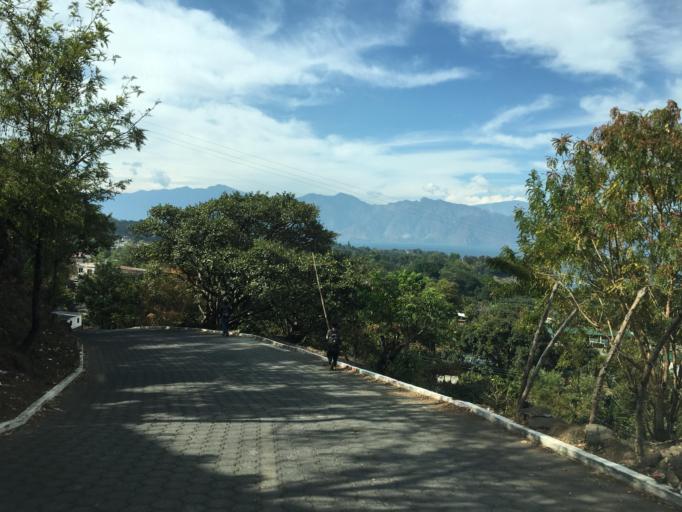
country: GT
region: Solola
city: San Antonio Palopo
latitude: 14.6589
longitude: -91.1576
